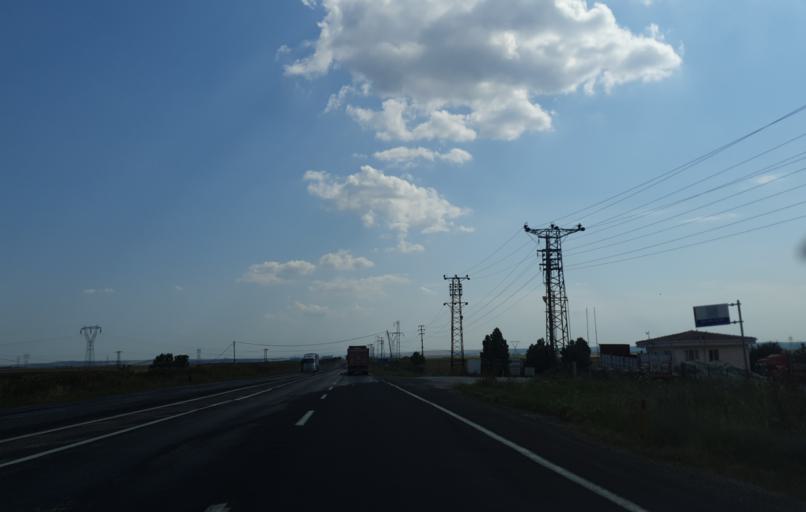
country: TR
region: Kirklareli
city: Buyukkaristiran
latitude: 41.2454
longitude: 27.5397
